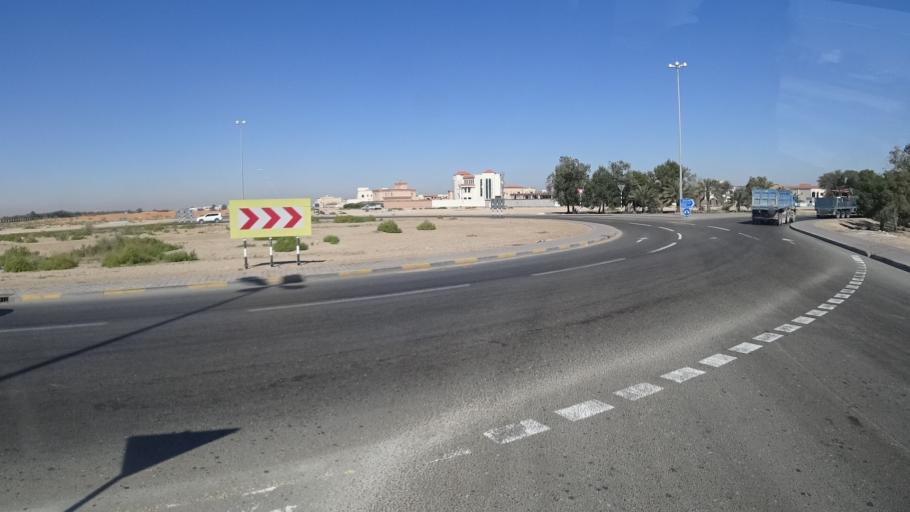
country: AE
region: Abu Dhabi
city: Al Ain
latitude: 24.1021
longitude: 55.6945
